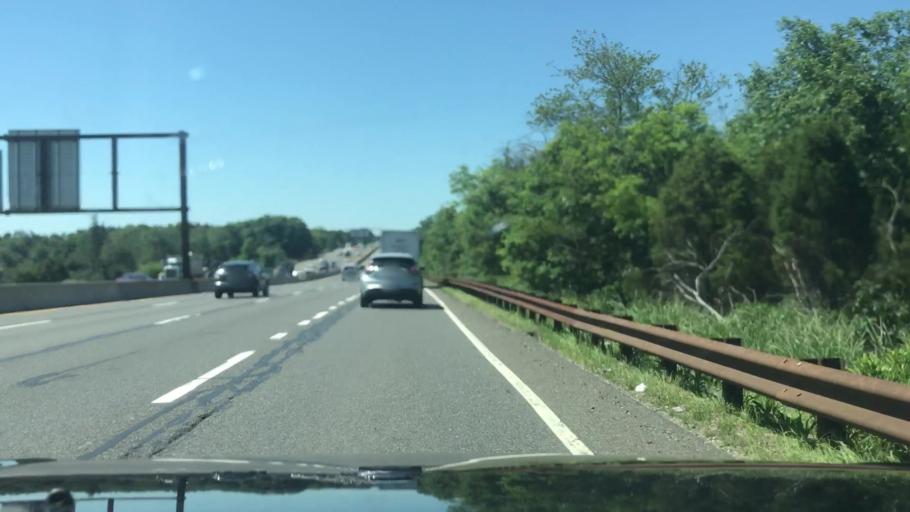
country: US
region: New Jersey
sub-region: Ocean County
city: South Toms River
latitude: 39.9513
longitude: -74.2074
